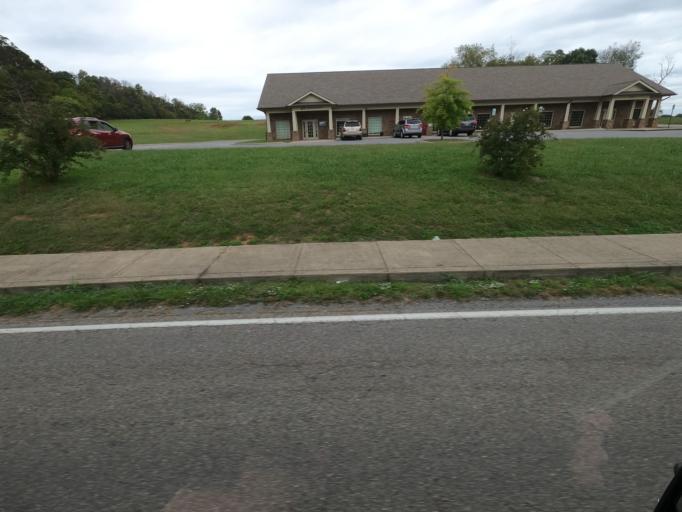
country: US
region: Tennessee
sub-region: Washington County
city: Oak Grove
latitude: 36.3879
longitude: -82.4157
